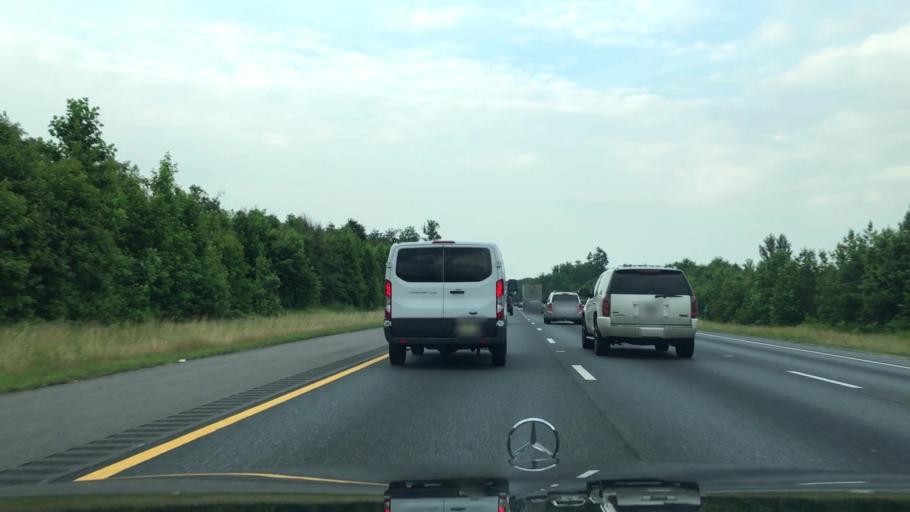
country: US
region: Virginia
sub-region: Stafford County
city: Stafford
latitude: 38.3889
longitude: -77.4433
